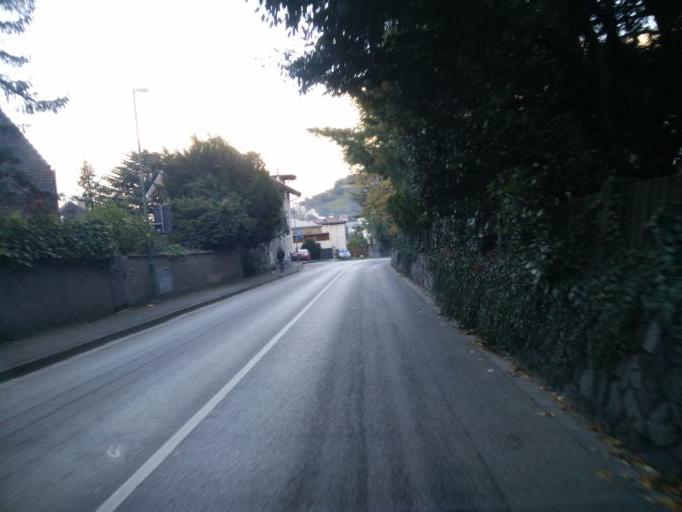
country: IT
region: Trentino-Alto Adige
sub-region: Bolzano
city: Merano
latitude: 46.6696
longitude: 11.1778
